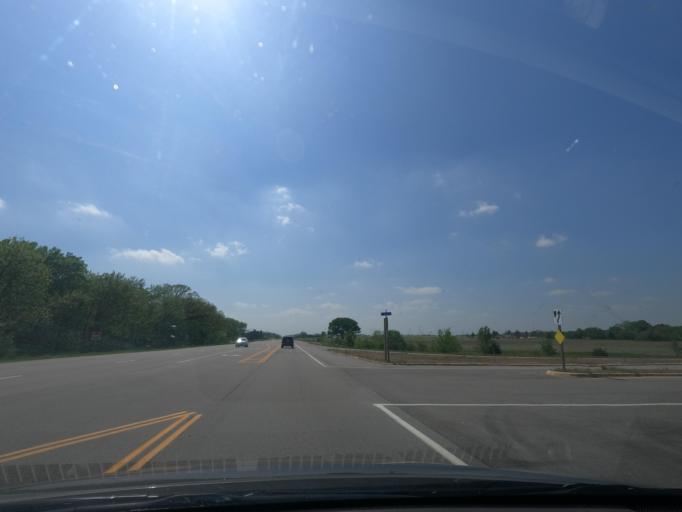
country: US
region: Kansas
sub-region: Butler County
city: El Dorado
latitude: 37.6796
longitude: -96.7821
